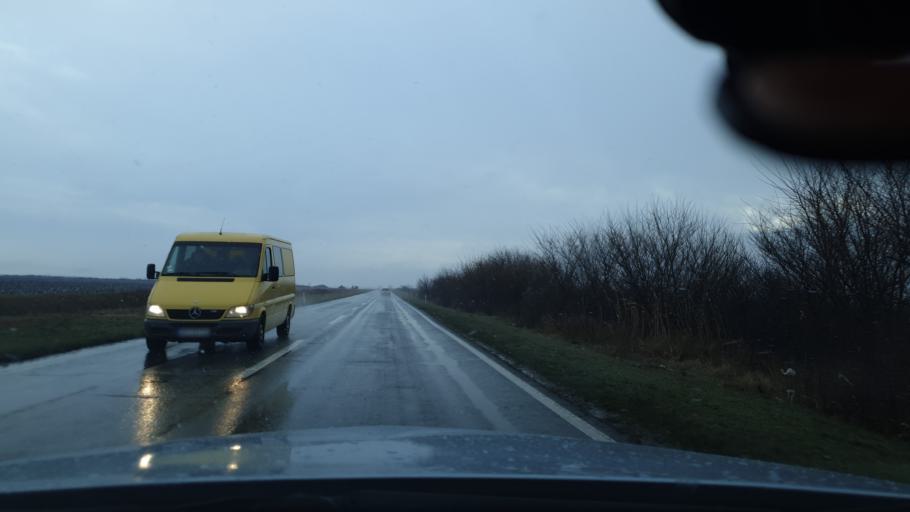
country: RS
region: Autonomna Pokrajina Vojvodina
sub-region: Juznobanatski Okrug
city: Pancevo
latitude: 44.8473
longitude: 20.7806
